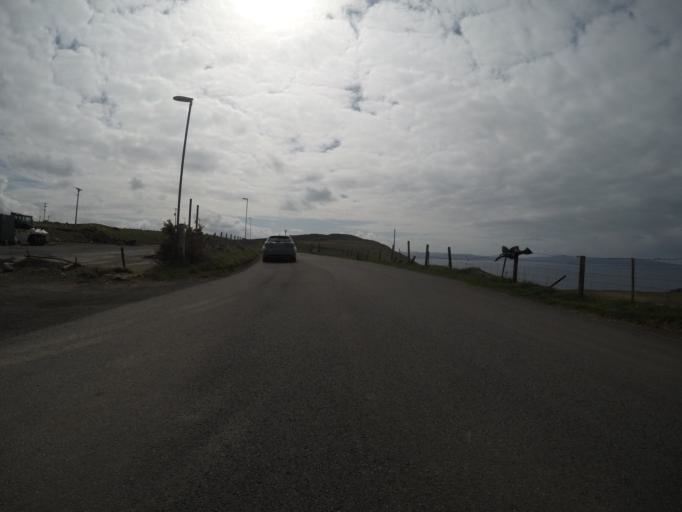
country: GB
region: Scotland
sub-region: Highland
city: Portree
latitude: 57.6034
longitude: -6.3773
